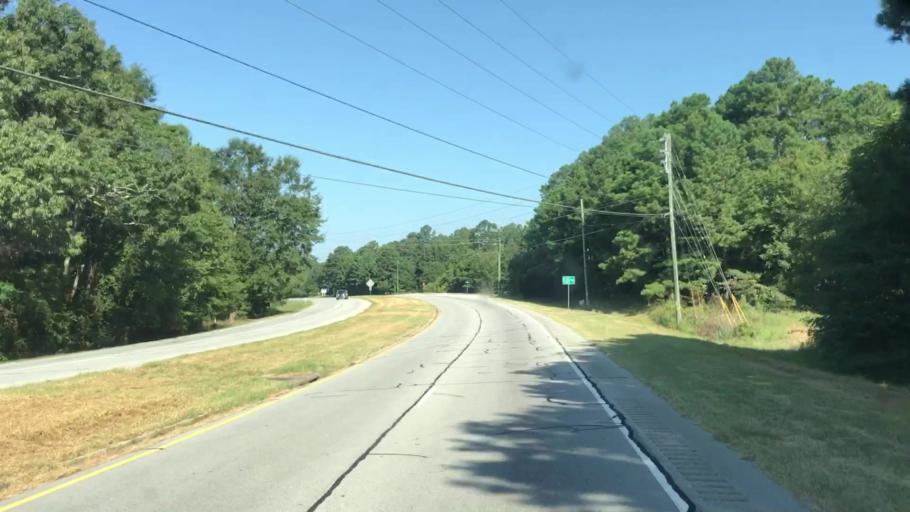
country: US
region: Georgia
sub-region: Walton County
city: Walnut Grove
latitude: 33.8191
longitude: -83.8090
